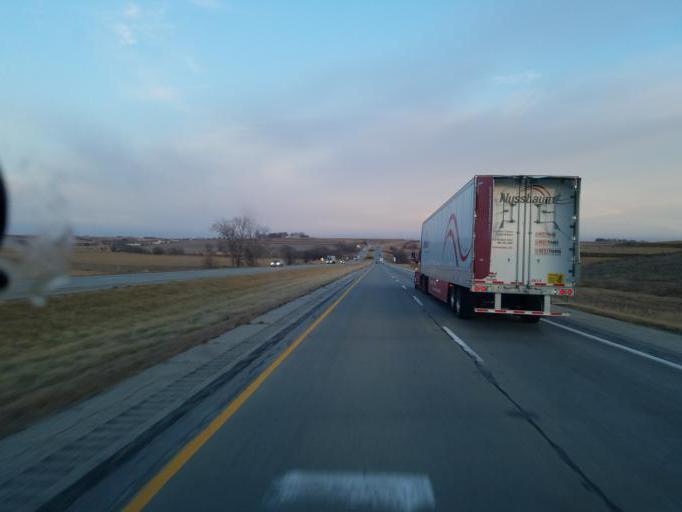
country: US
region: Iowa
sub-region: Pottawattamie County
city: Avoca
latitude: 41.4987
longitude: -95.5386
